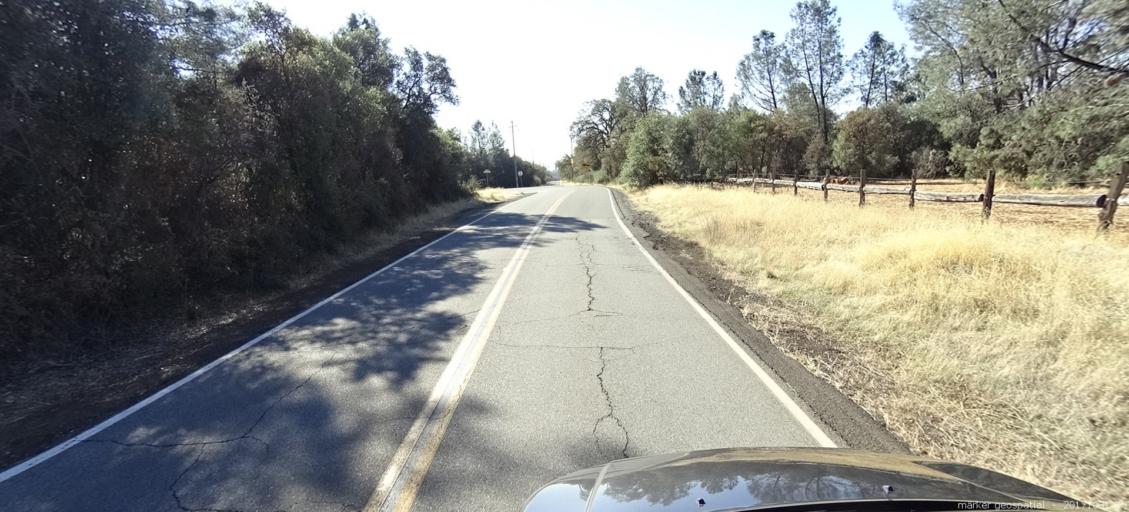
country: US
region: California
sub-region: Shasta County
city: Shingletown
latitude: 40.4468
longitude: -121.8994
